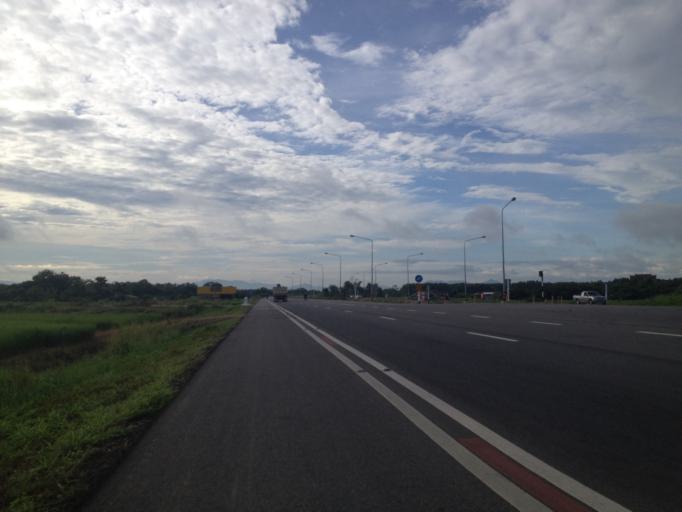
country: TH
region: Chiang Mai
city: San Pa Tong
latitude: 18.5717
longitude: 98.8473
